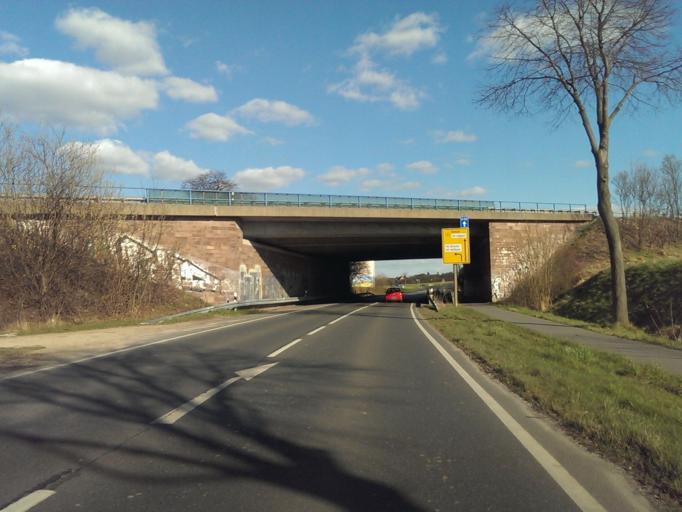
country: DE
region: Lower Saxony
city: Hildesheim
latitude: 52.1474
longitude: 9.9937
